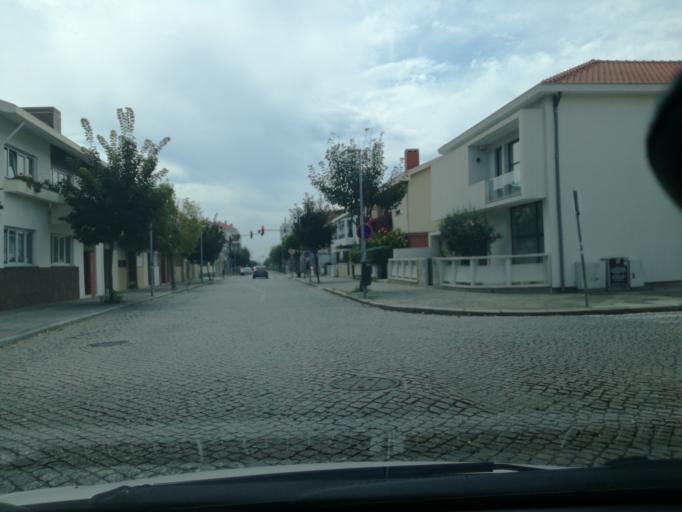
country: PT
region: Aveiro
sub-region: Espinho
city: Espinho
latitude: 41.0048
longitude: -8.6399
